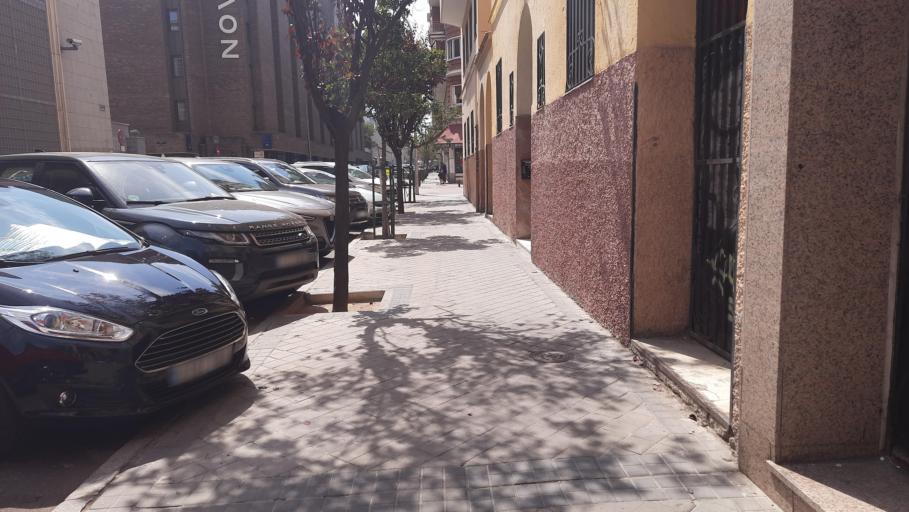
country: ES
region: Madrid
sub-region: Provincia de Madrid
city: Salamanca
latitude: 40.4227
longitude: -3.6728
